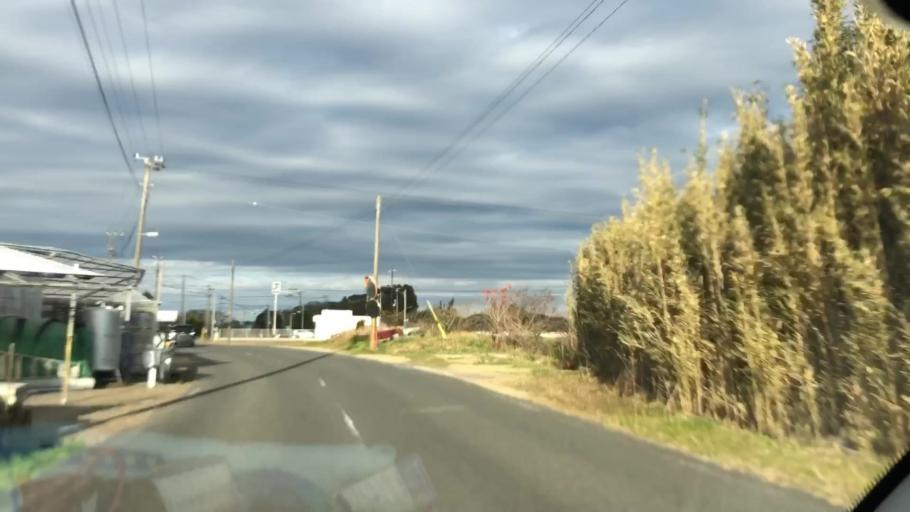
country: JP
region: Chiba
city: Tateyama
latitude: 35.0059
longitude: 139.8817
